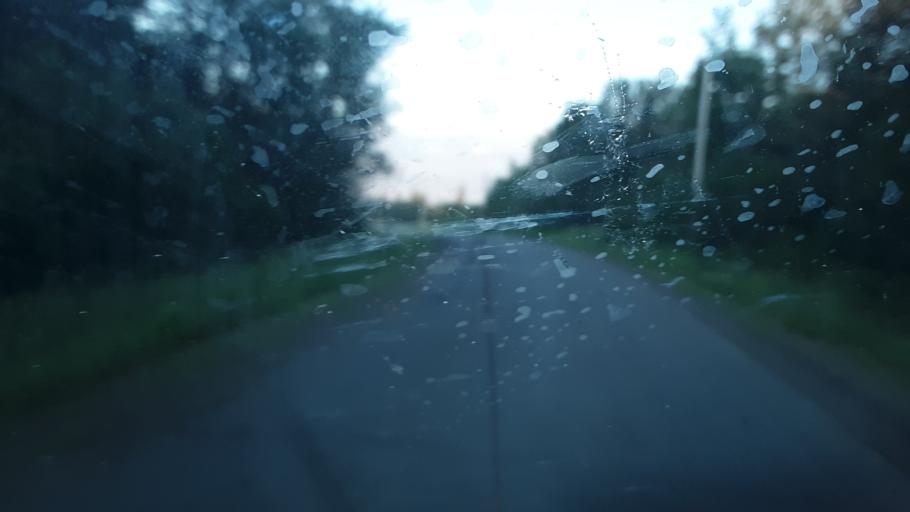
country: US
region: Maine
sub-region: Aroostook County
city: Caribou
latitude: 46.8462
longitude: -68.1380
